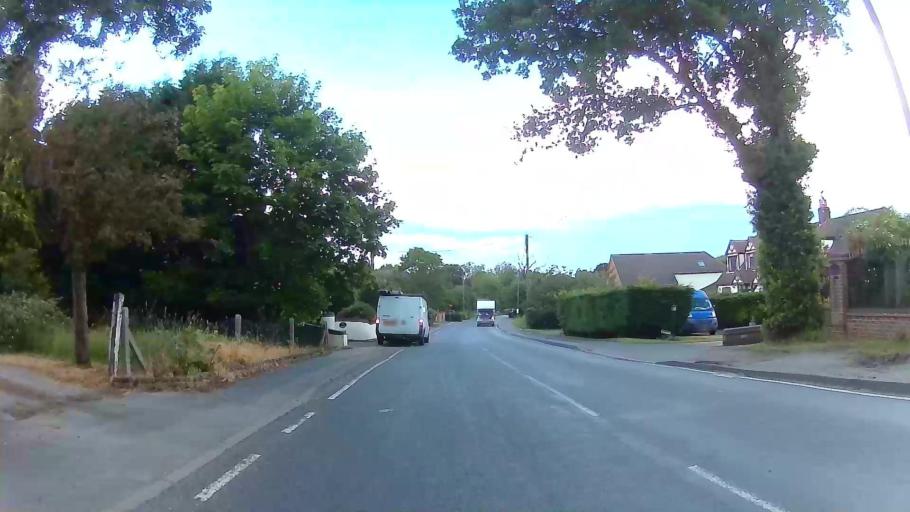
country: GB
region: England
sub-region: Greater London
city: Collier Row
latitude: 51.6289
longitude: 0.1876
